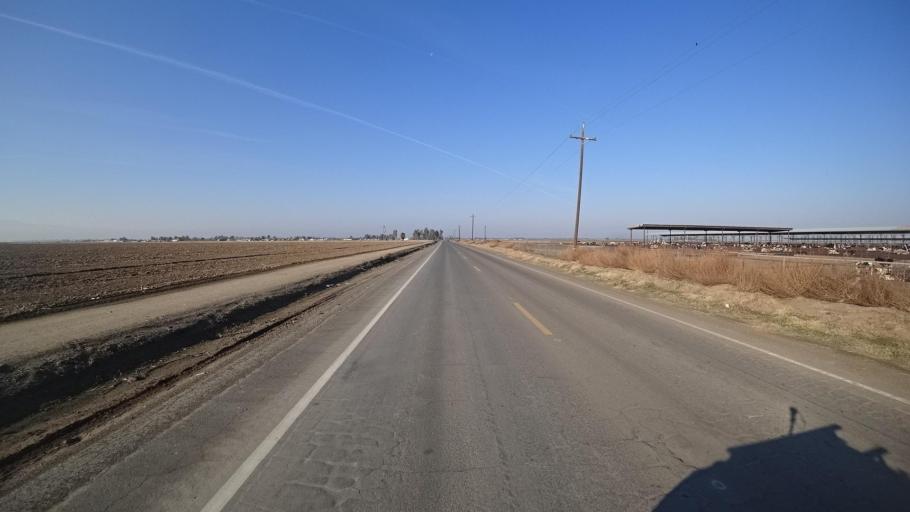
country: US
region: California
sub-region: Kern County
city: Lamont
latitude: 35.2524
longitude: -118.9472
